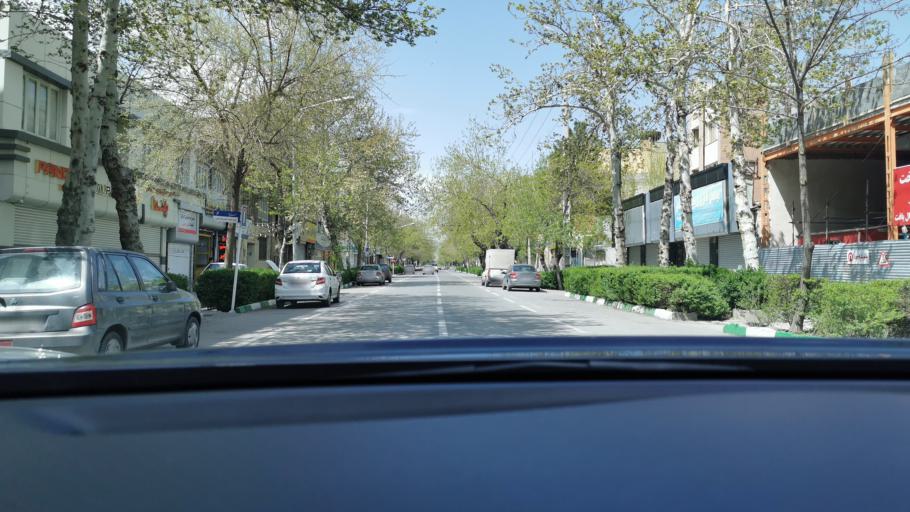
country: IR
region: Razavi Khorasan
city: Mashhad
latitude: 36.2969
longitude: 59.5960
